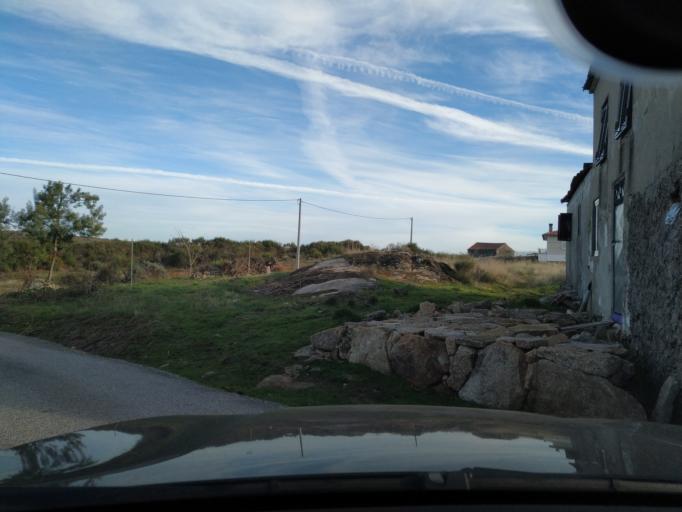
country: PT
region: Vila Real
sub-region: Sabrosa
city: Sabrosa
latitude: 41.3054
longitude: -7.6109
